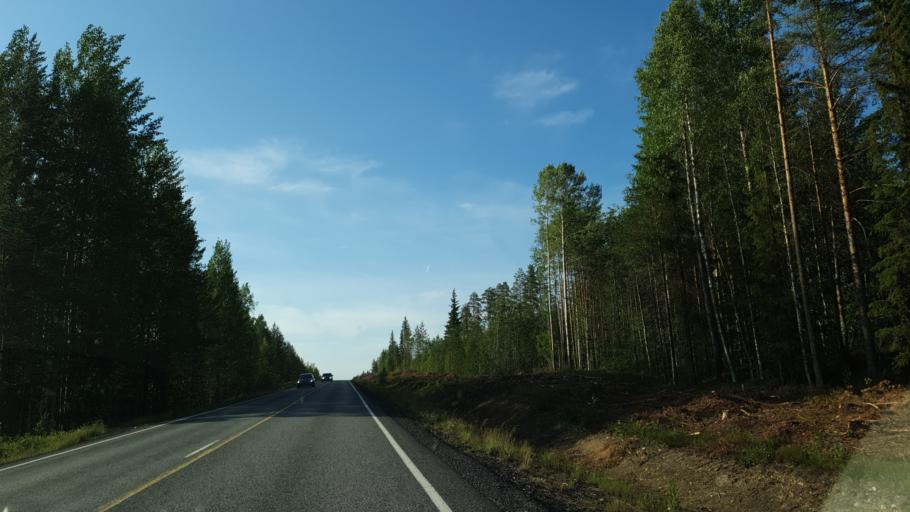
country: FI
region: Kainuu
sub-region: Kehys-Kainuu
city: Kuhmo
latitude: 64.0830
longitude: 29.4847
